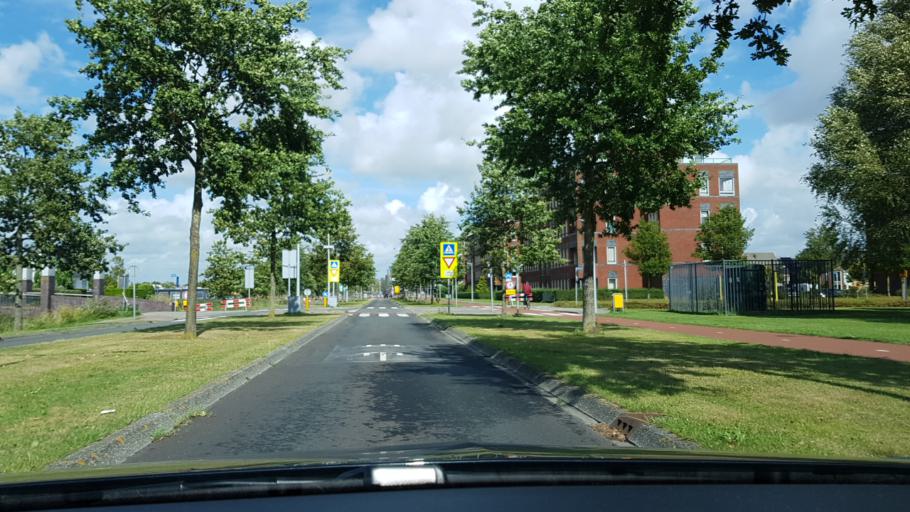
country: NL
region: North Holland
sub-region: Gemeente Bloemendaal
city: Bennebroek
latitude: 52.3039
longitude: 4.6414
